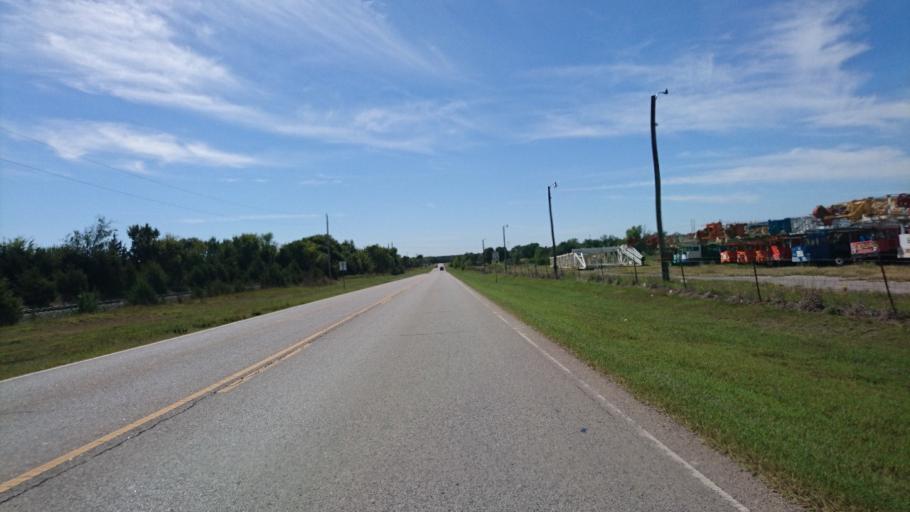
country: US
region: Oklahoma
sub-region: Lincoln County
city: Stroud
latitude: 35.7441
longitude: -96.6991
